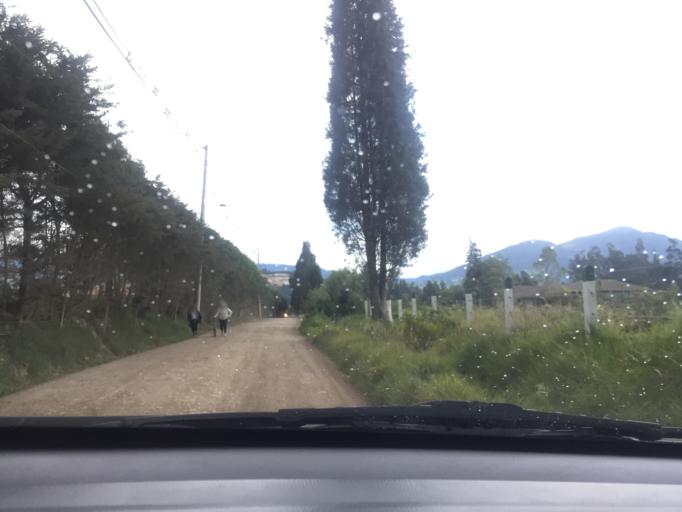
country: CO
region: Cundinamarca
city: Cogua
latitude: 5.0662
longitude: -73.9312
